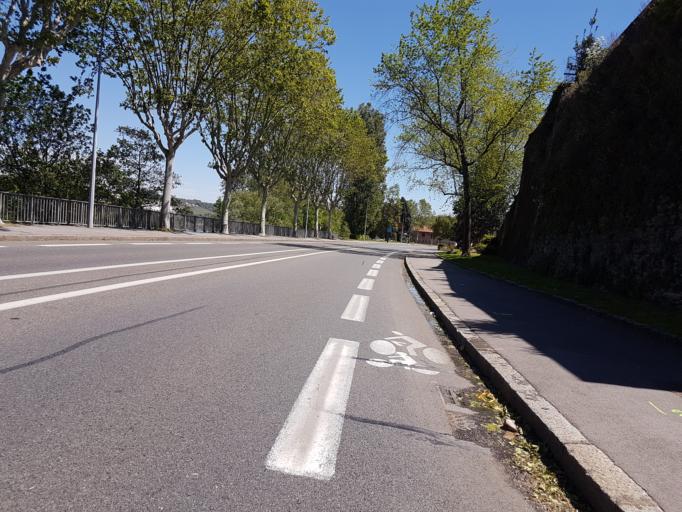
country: FR
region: Rhone-Alpes
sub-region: Departement du Rhone
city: Givors
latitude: 45.5773
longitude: 4.7837
